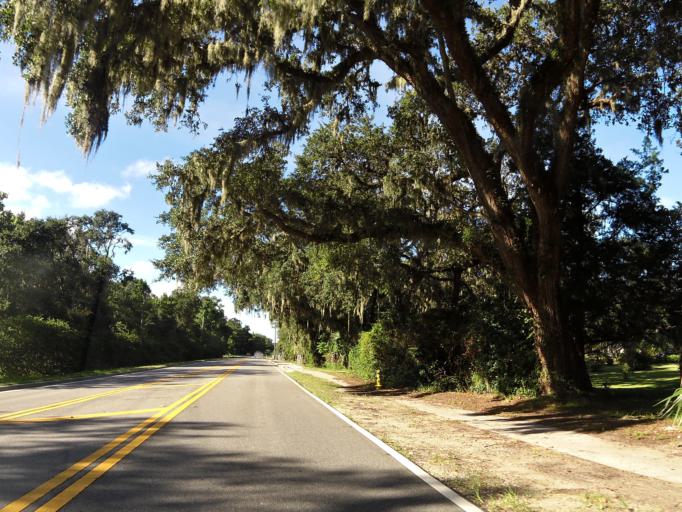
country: US
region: Florida
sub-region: Nassau County
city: Fernandina Beach
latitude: 30.6246
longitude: -81.4553
